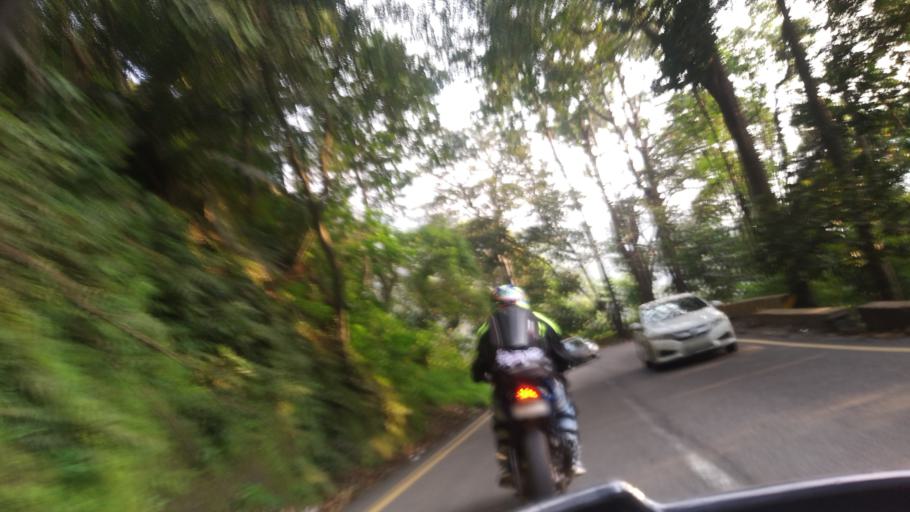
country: IN
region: Kerala
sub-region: Wayanad
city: Kalpetta
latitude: 11.5084
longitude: 76.0283
